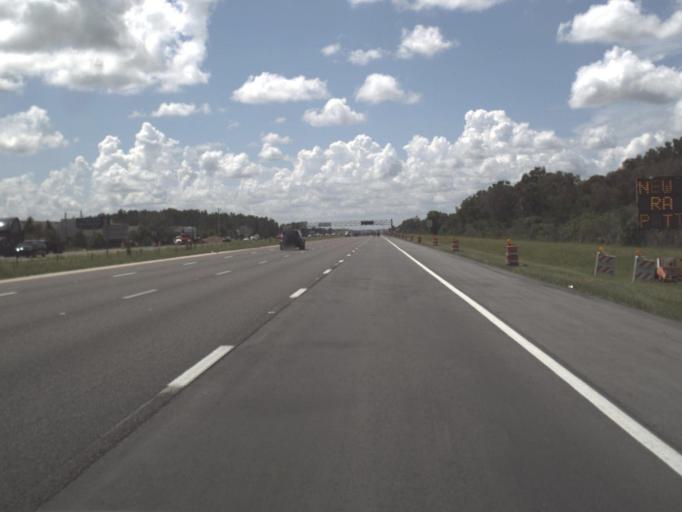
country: US
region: Florida
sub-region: Lee County
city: Gateway
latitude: 26.5381
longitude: -81.7951
